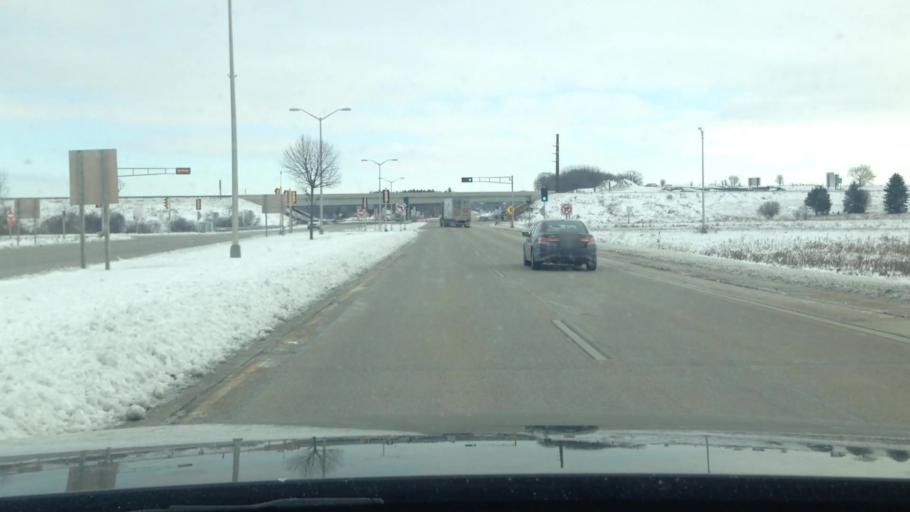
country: US
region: Wisconsin
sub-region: Walworth County
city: Lake Geneva
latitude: 42.5934
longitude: -88.4120
